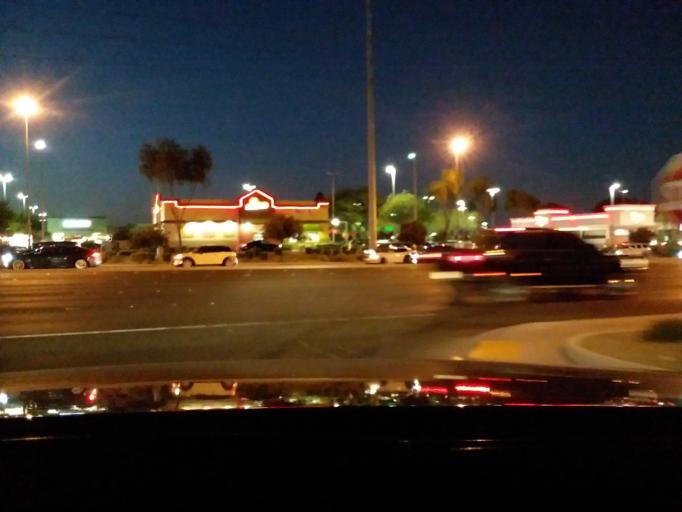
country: US
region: Nevada
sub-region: Clark County
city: Enterprise
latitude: 36.0395
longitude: -115.1917
